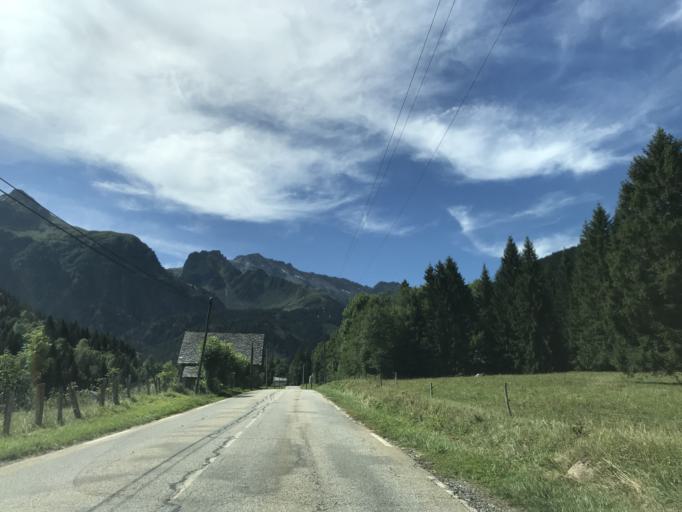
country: FR
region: Rhone-Alpes
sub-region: Departement de l'Isere
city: Theys
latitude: 45.2941
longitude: 6.0779
